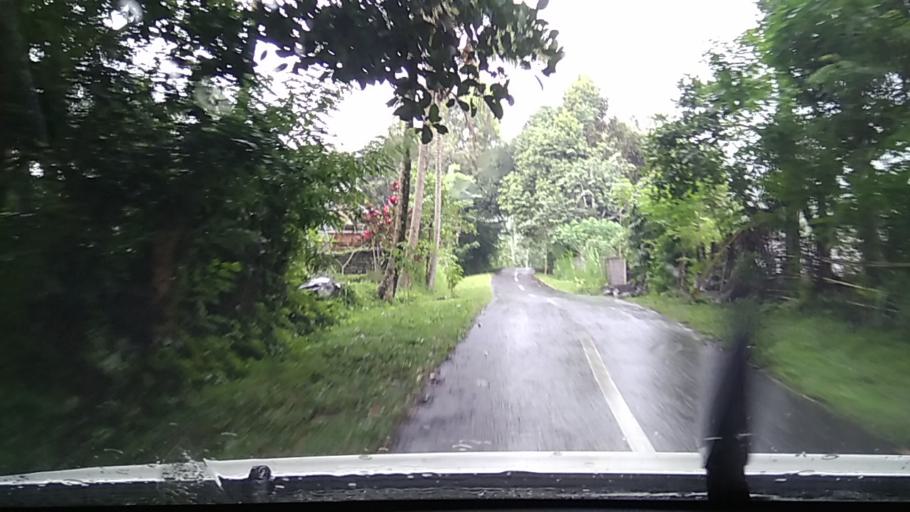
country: ID
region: Bali
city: Tiyingtali Kelod
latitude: -8.4048
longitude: 115.6278
